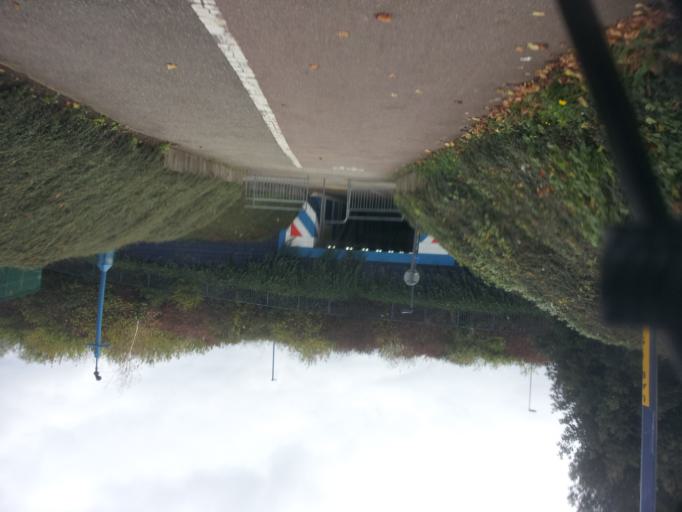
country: GB
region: England
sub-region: Kent
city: Gillingham
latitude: 51.3711
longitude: 0.5699
